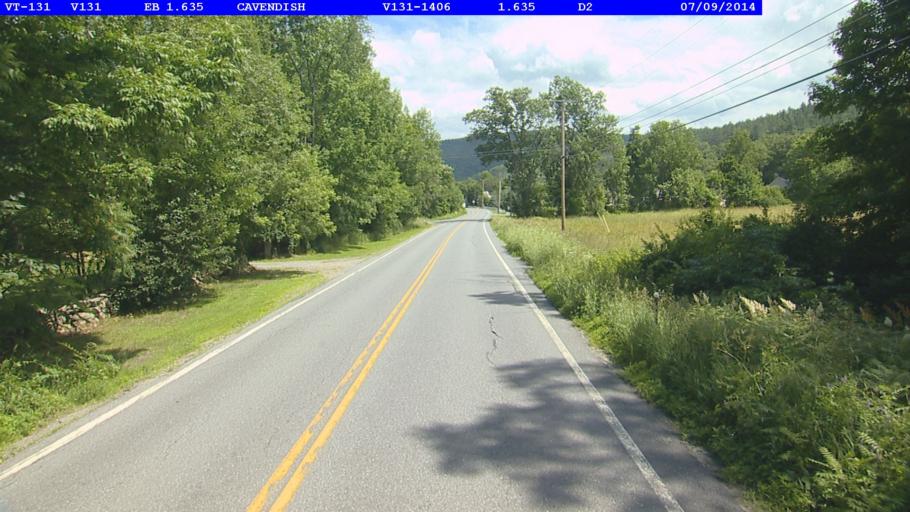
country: US
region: Vermont
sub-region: Windsor County
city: Chester
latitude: 43.3839
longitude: -72.6168
